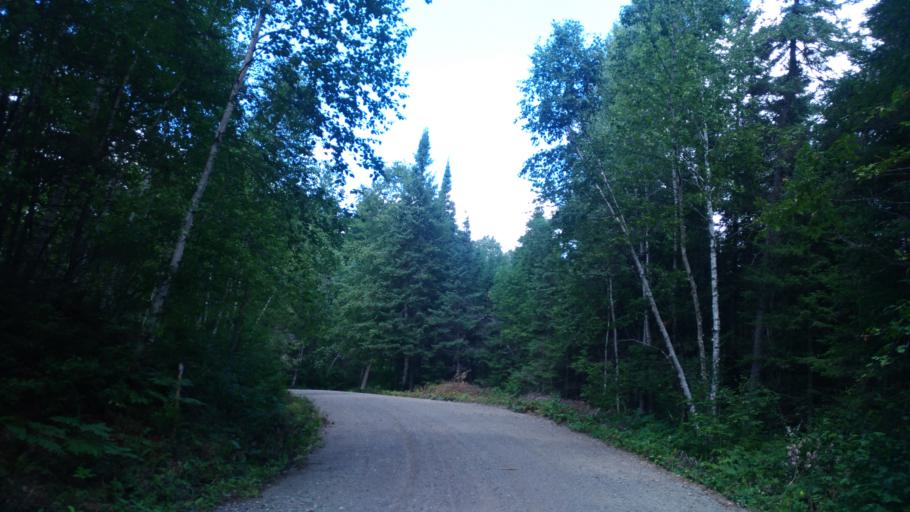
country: CA
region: Ontario
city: Rayside-Balfour
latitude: 46.5903
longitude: -81.5477
